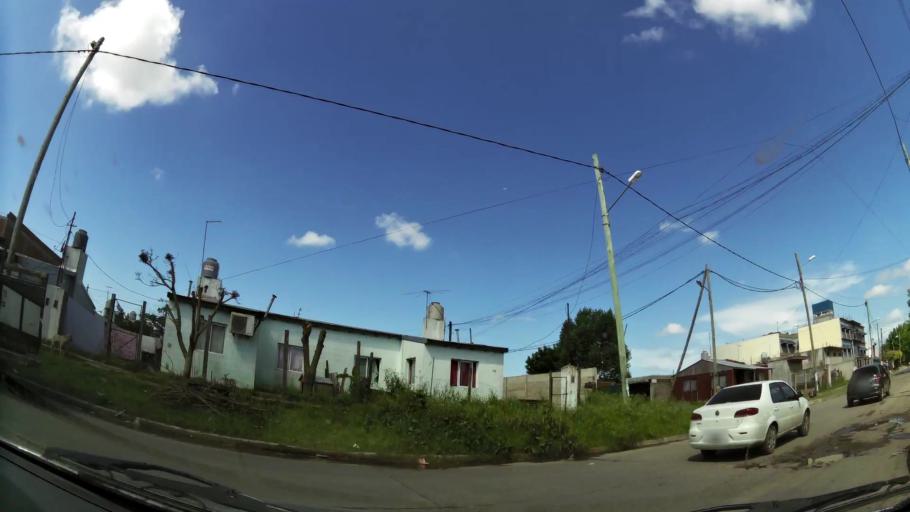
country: AR
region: Buenos Aires
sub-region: Partido de Quilmes
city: Quilmes
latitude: -34.8034
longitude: -58.2649
